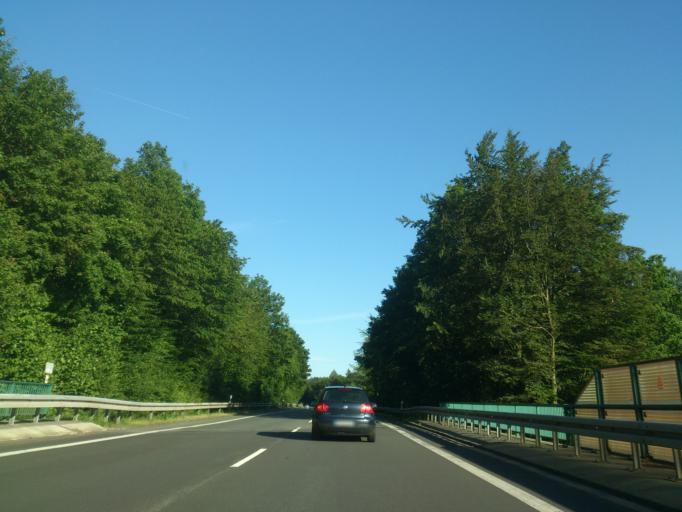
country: DE
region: North Rhine-Westphalia
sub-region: Regierungsbezirk Detmold
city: Altenbeken
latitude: 51.6976
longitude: 8.9544
